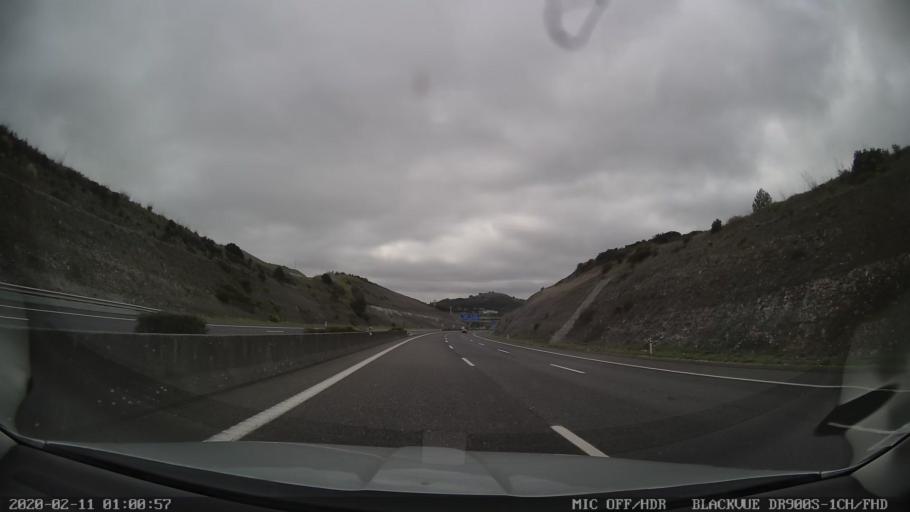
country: PT
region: Lisbon
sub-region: Vila Franca de Xira
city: Vialonga
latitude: 38.9159
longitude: -9.0729
